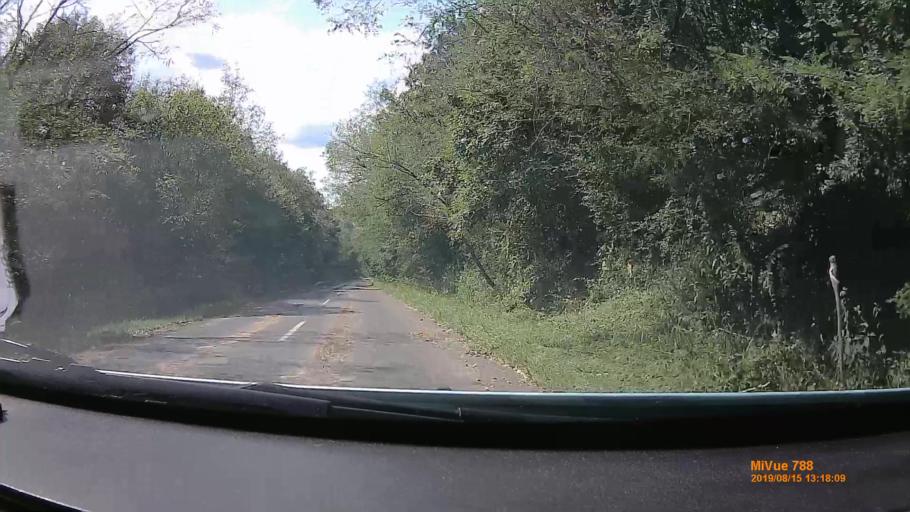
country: HU
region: Borsod-Abauj-Zemplen
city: Sajobabony
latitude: 48.1572
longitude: 20.6465
